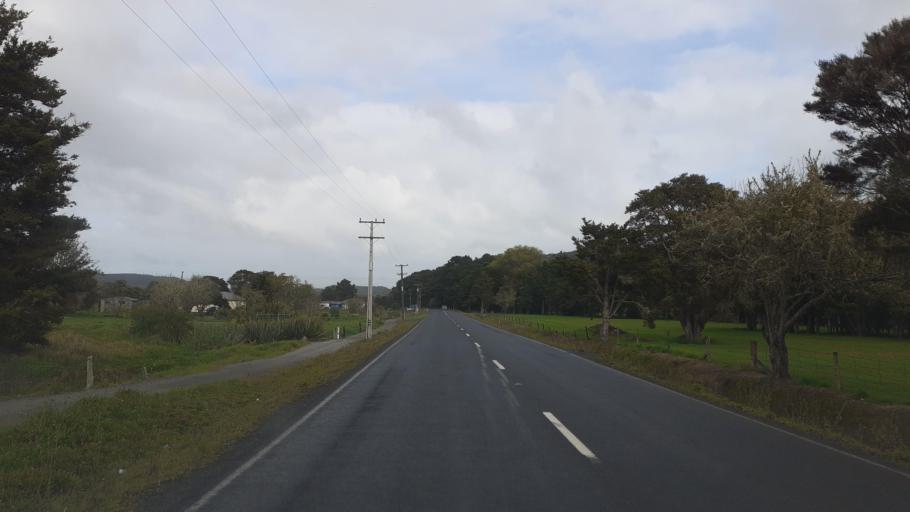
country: NZ
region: Northland
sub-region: Far North District
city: Moerewa
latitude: -35.3985
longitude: 173.9972
